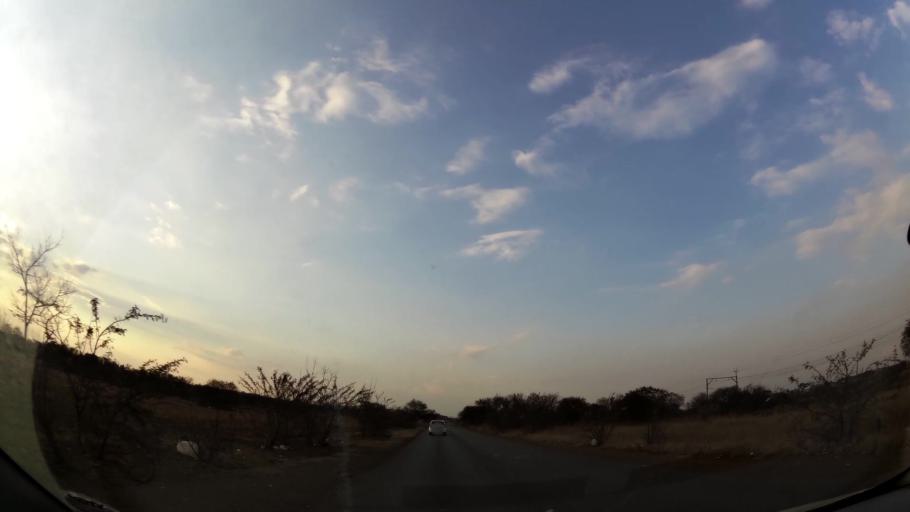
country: ZA
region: Gauteng
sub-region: City of Johannesburg Metropolitan Municipality
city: Orange Farm
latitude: -26.5717
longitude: 27.8595
